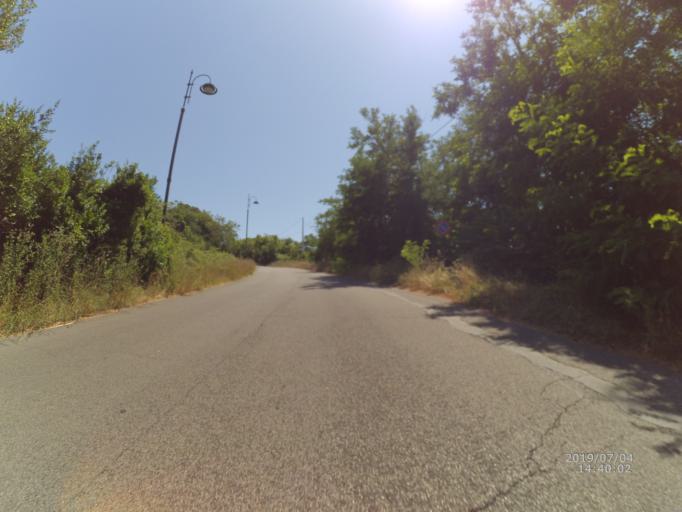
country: IT
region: Latium
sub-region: Provincia di Latina
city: Gaeta
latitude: 41.2112
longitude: 13.5729
